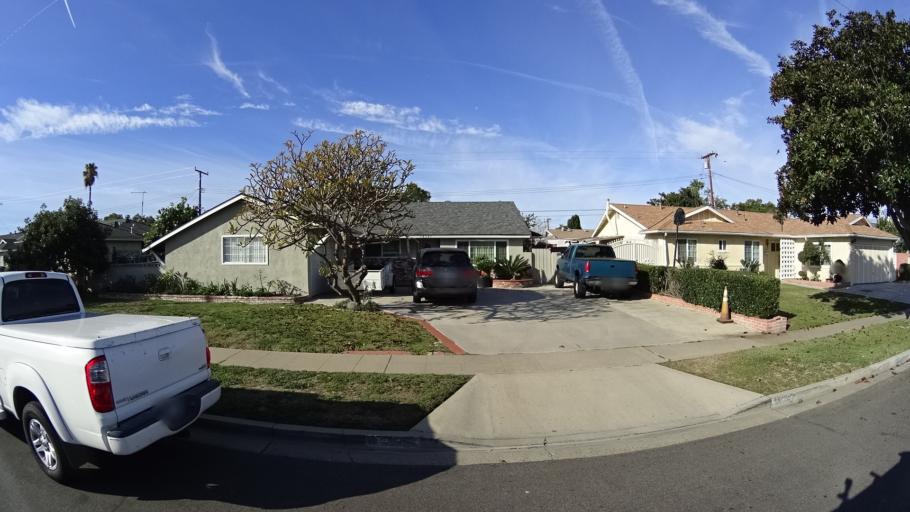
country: US
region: California
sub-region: Orange County
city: Garden Grove
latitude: 33.7546
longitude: -117.9424
